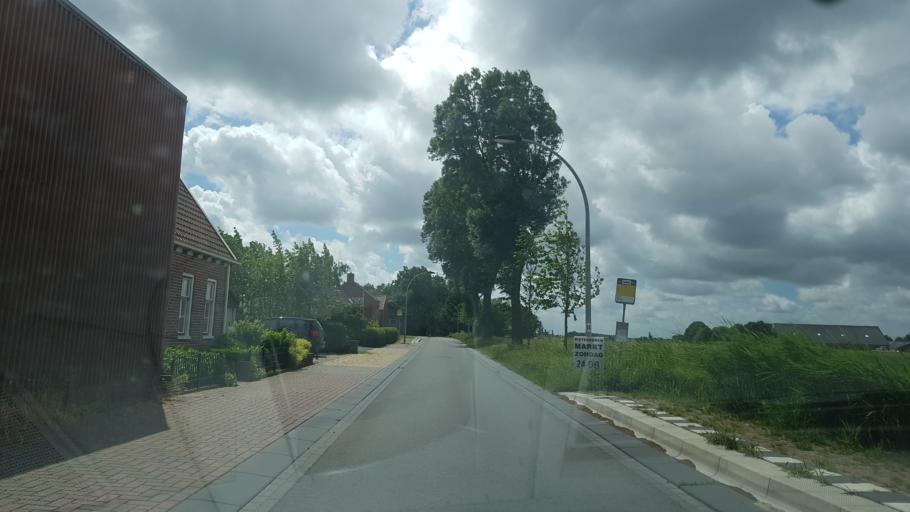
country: NL
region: Groningen
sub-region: Gemeente Winsum
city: Winsum
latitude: 53.3934
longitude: 6.5072
